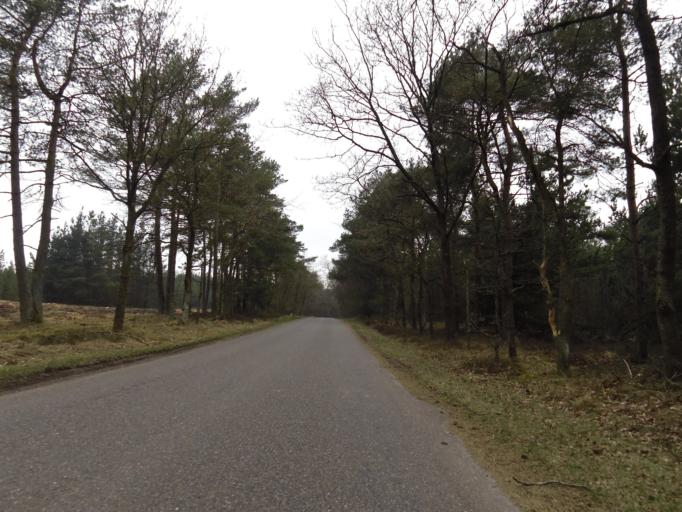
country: DK
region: Central Jutland
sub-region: Holstebro Kommune
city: Vinderup
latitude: 56.5147
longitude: 8.8387
